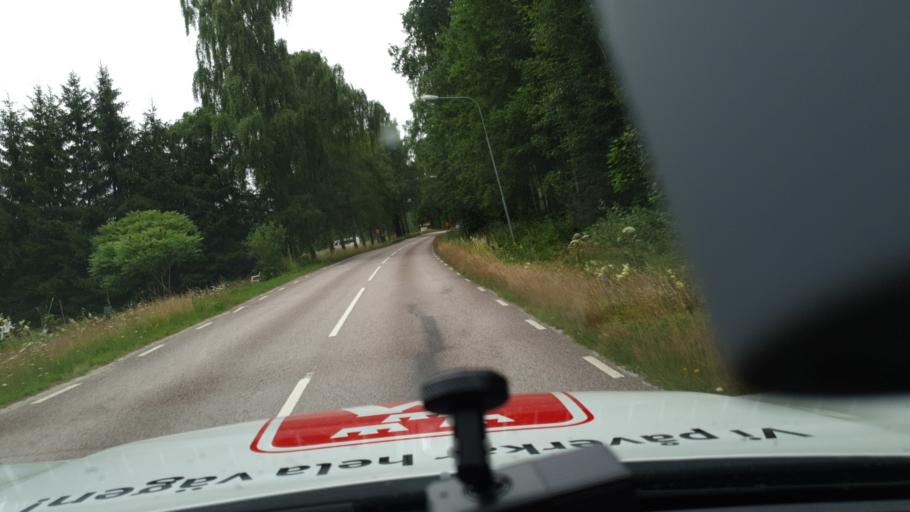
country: SE
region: Vaermland
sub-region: Sunne Kommun
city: Sunne
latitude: 59.7784
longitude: 13.2353
